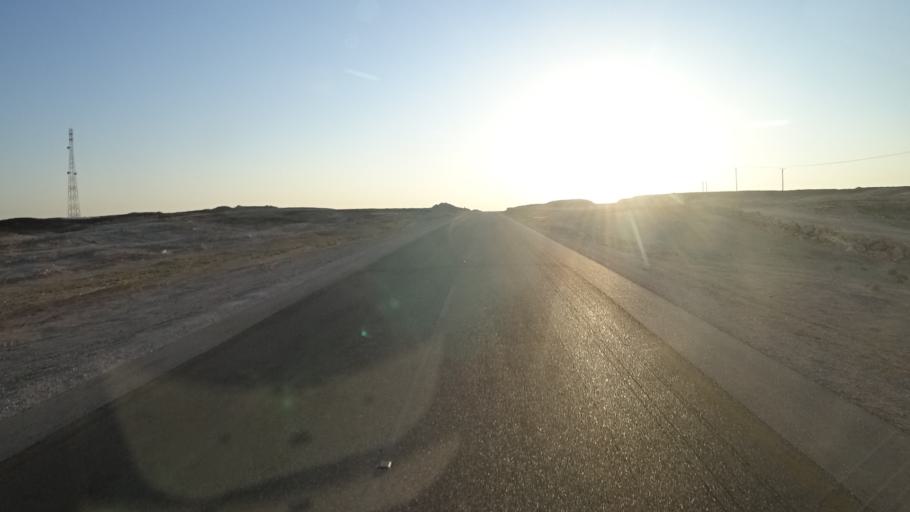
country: OM
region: Zufar
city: Salalah
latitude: 17.5398
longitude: 53.4147
